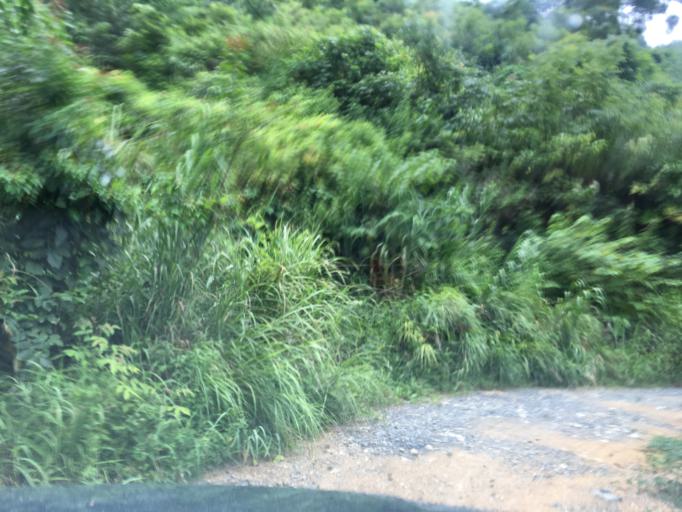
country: CN
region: Guangxi Zhuangzu Zizhiqu
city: Tongle
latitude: 25.0049
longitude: 105.9875
